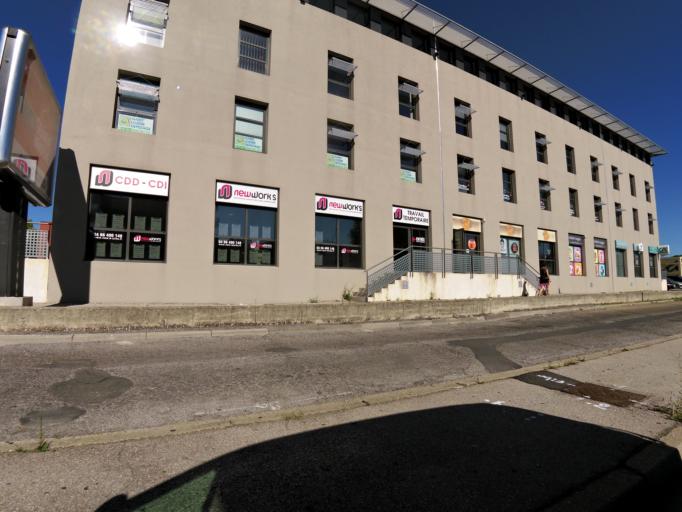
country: FR
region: Languedoc-Roussillon
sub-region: Departement du Gard
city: Nimes
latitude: 43.8228
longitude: 4.3645
